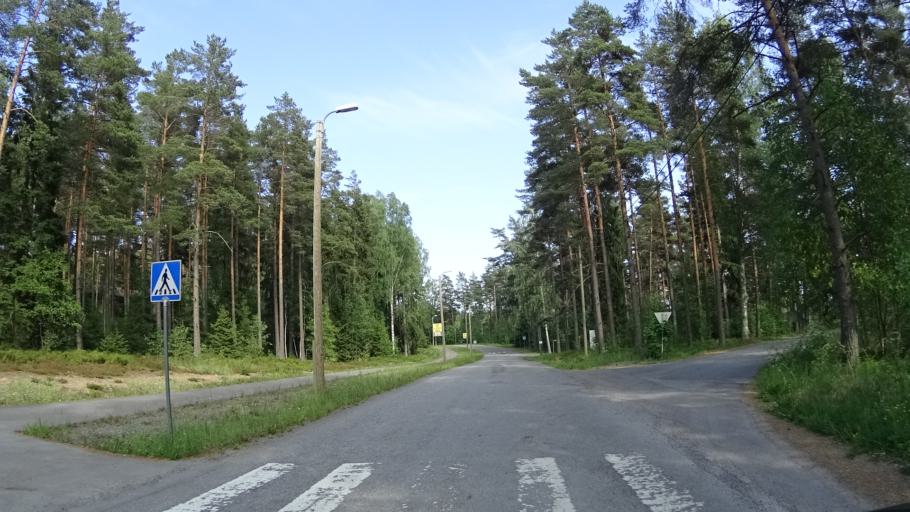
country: FI
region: Uusimaa
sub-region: Raaseporin
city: Inga
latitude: 60.0549
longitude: 23.9854
